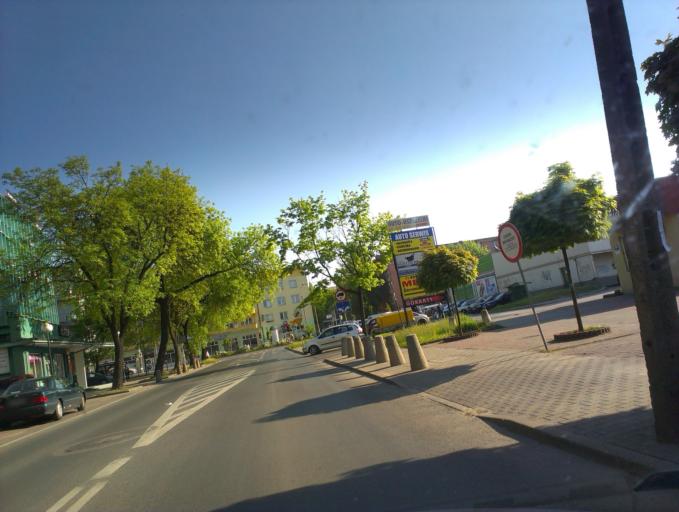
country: PL
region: Masovian Voivodeship
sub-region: Radom
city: Radom
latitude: 51.3988
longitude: 21.1668
